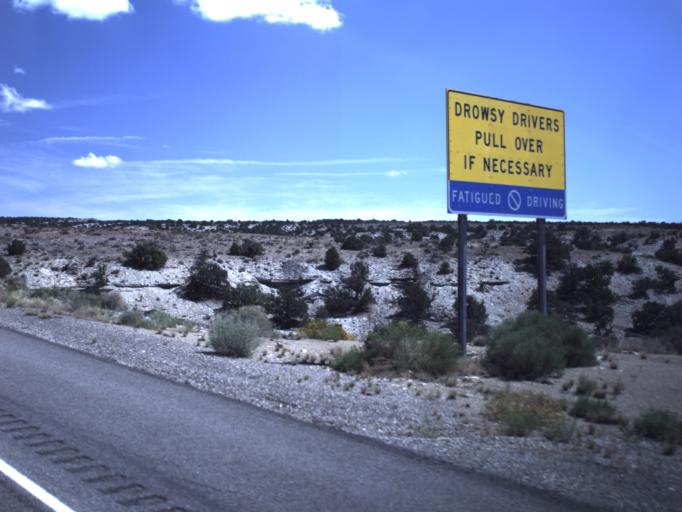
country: US
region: Utah
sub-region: Emery County
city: Ferron
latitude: 38.8429
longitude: -110.9713
